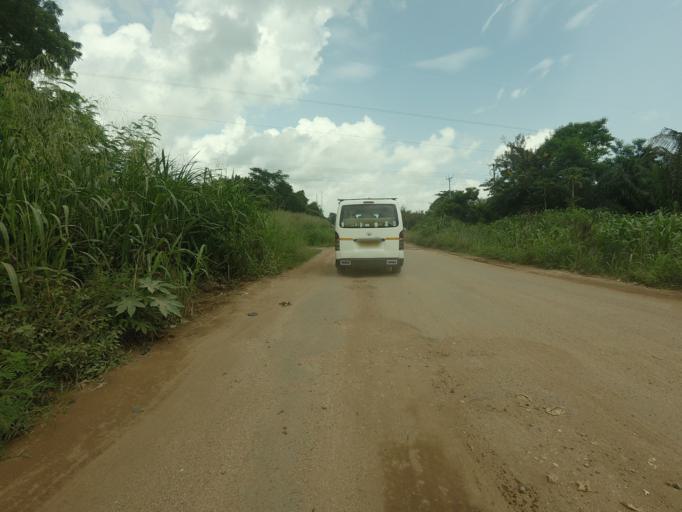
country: GH
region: Volta
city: Ho
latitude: 6.6924
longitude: 0.3354
